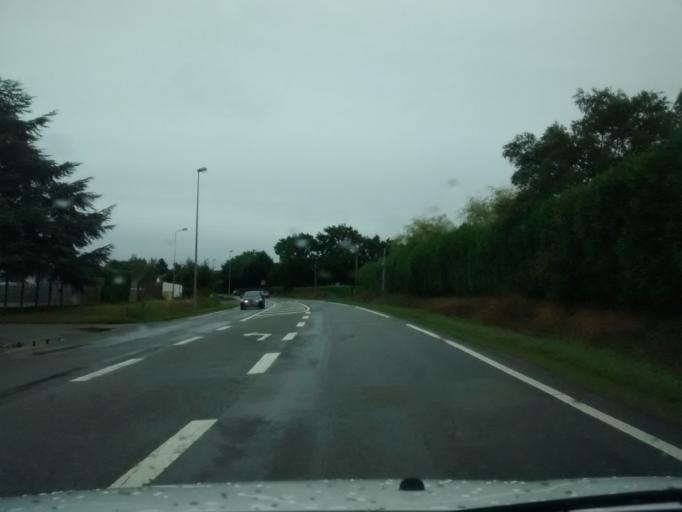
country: FR
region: Brittany
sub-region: Departement d'Ille-et-Vilaine
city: Vern-sur-Seiche
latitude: 48.0507
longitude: -1.6017
